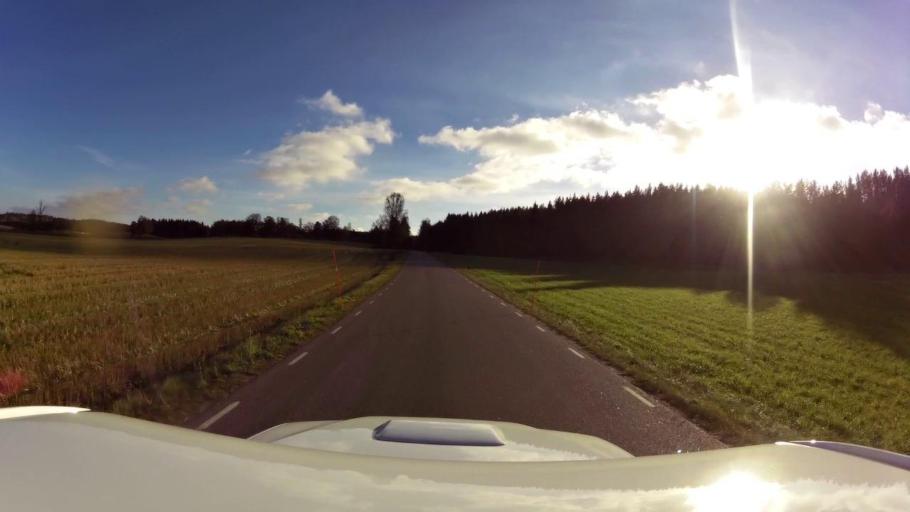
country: SE
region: OEstergoetland
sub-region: Linkopings Kommun
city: Vikingstad
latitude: 58.2770
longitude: 15.4347
